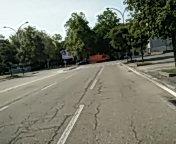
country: IT
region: Piedmont
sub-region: Provincia di Torino
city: Nichelino
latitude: 45.0278
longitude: 7.6496
